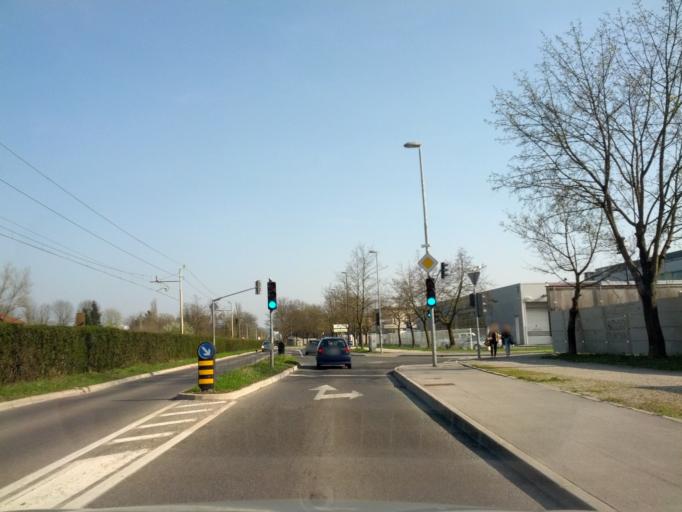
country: SI
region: Ljubljana
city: Ljubljana
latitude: 46.0796
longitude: 14.4871
